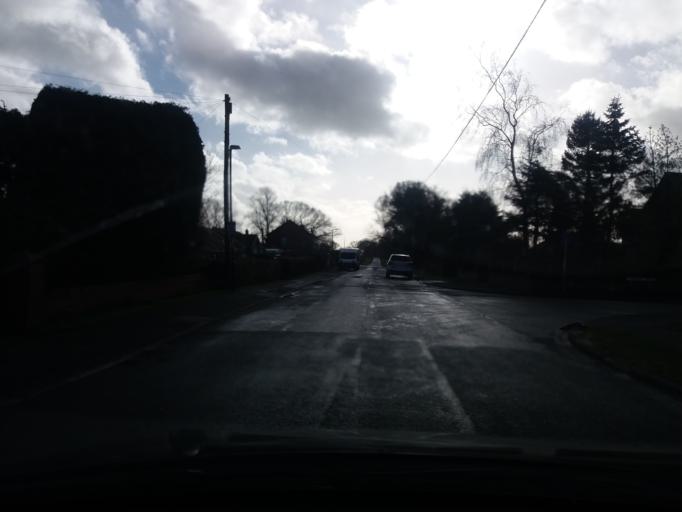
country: GB
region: England
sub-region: Lancashire
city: Adlington
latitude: 53.6079
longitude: -2.6153
